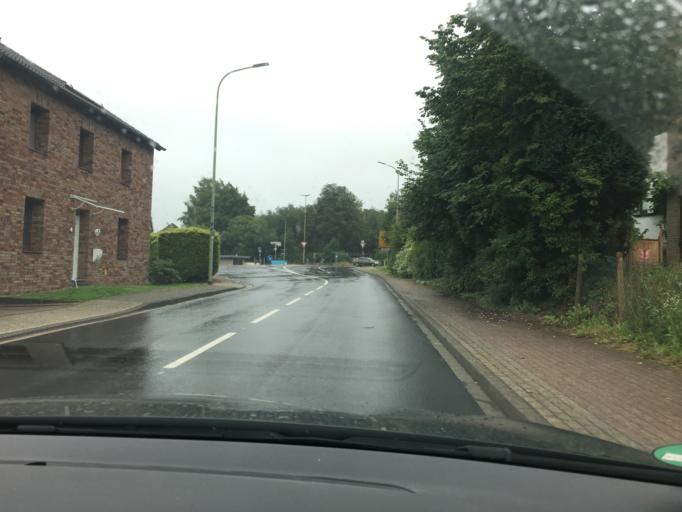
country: DE
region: North Rhine-Westphalia
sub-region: Regierungsbezirk Koln
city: Simmerath
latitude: 50.6327
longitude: 6.2727
